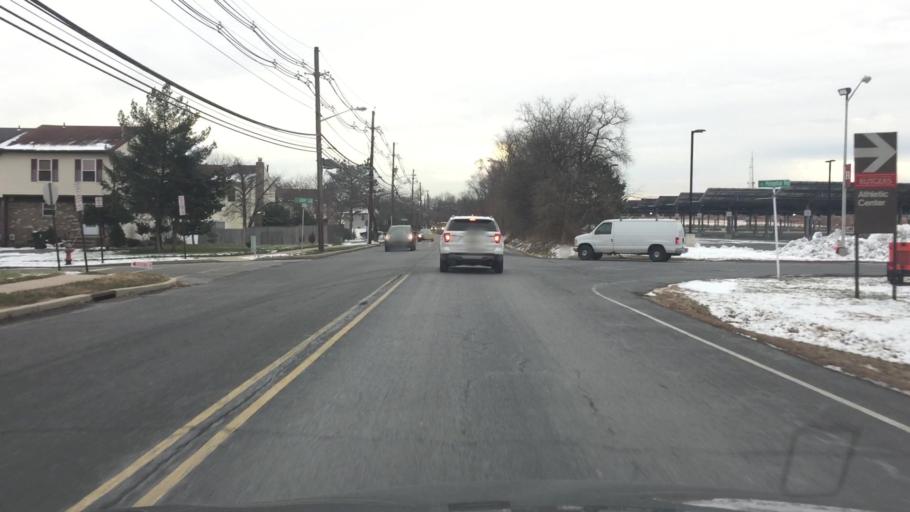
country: US
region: New Jersey
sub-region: Middlesex County
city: Society Hill
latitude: 40.5300
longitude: -74.4387
